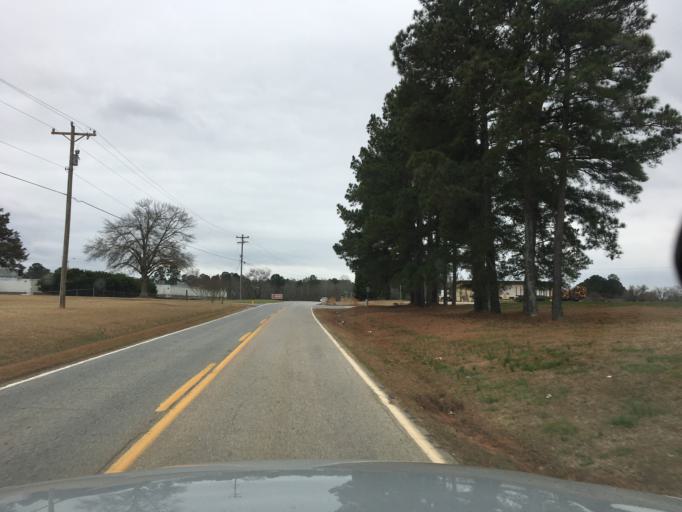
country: US
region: South Carolina
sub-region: Greenwood County
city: Greenwood
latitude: 34.2271
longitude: -82.1061
